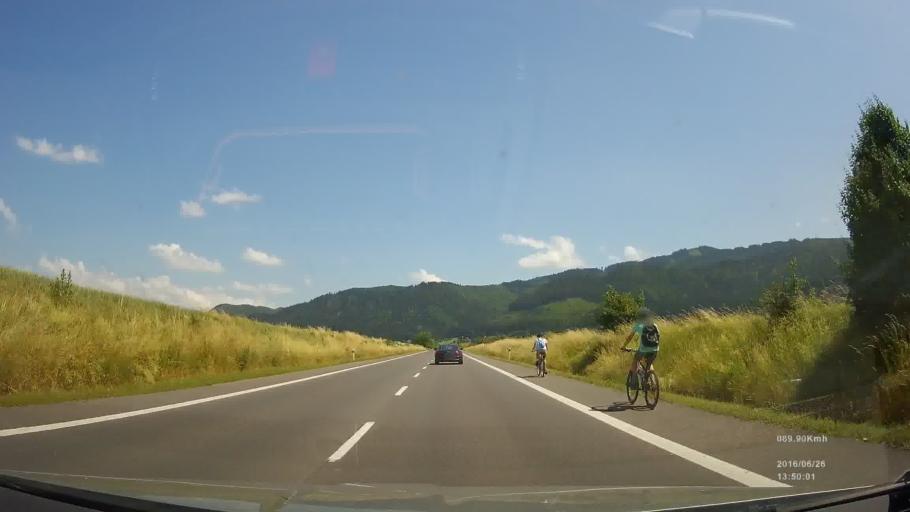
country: SK
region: Banskobystricky
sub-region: Okres Banska Bystrica
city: Brezno
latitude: 48.8142
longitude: 19.4470
